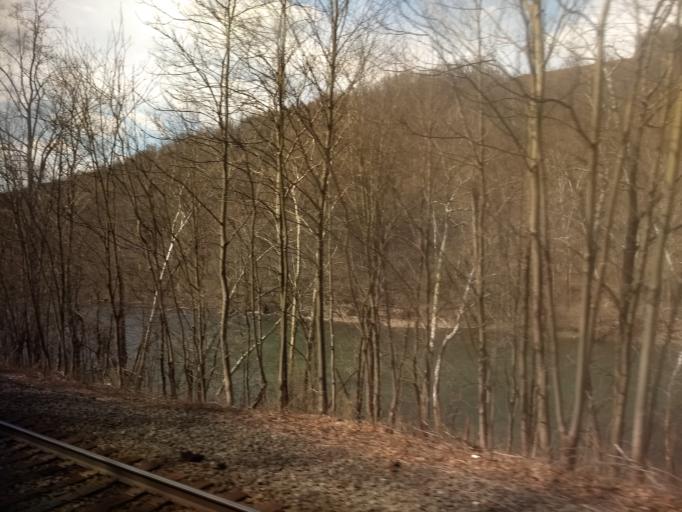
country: US
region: Pennsylvania
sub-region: Huntingdon County
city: Huntingdon
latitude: 40.5347
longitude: -78.0262
